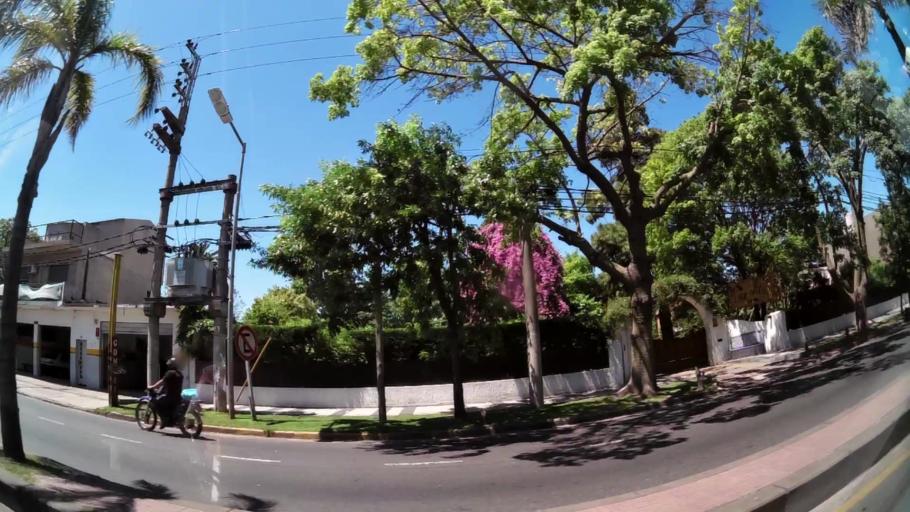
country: AR
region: Buenos Aires
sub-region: Partido de Tigre
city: Tigre
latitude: -34.4945
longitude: -58.6322
